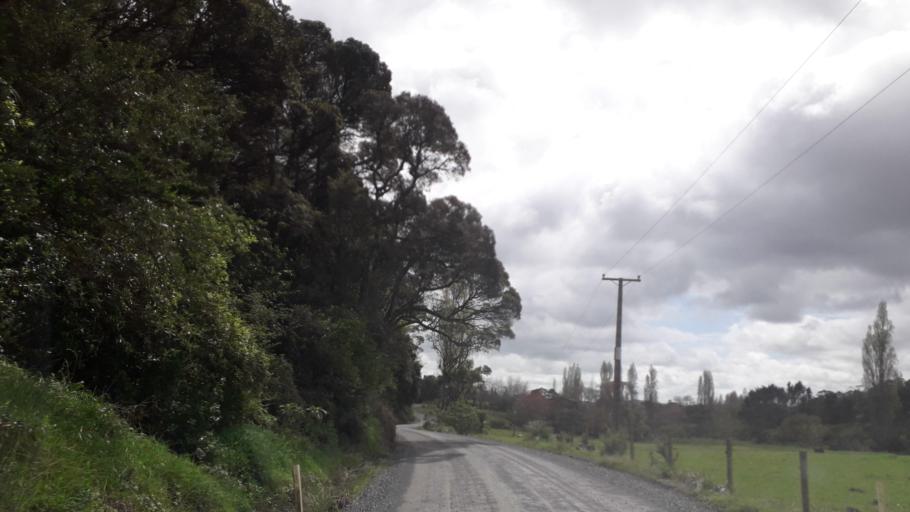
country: NZ
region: Northland
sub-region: Far North District
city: Kaitaia
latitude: -35.1653
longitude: 173.3442
